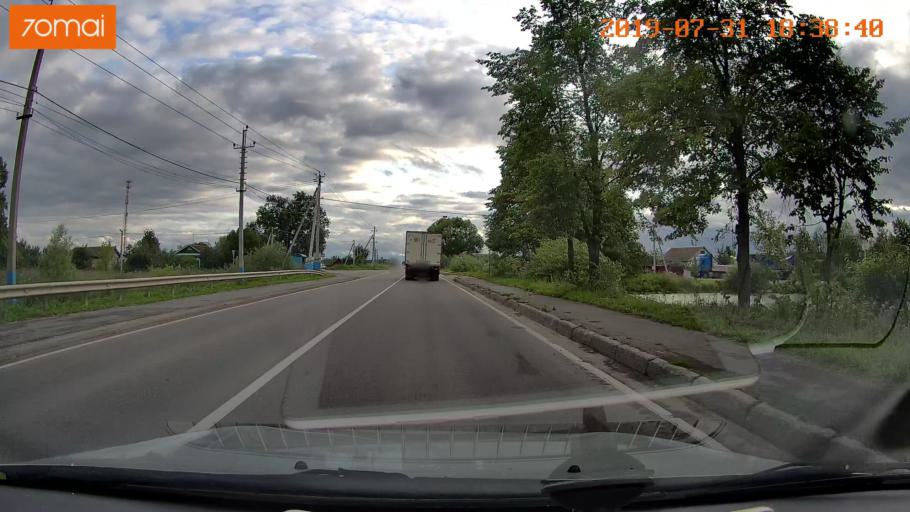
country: RU
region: Moskovskaya
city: Voskresensk
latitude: 55.2715
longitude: 38.6536
